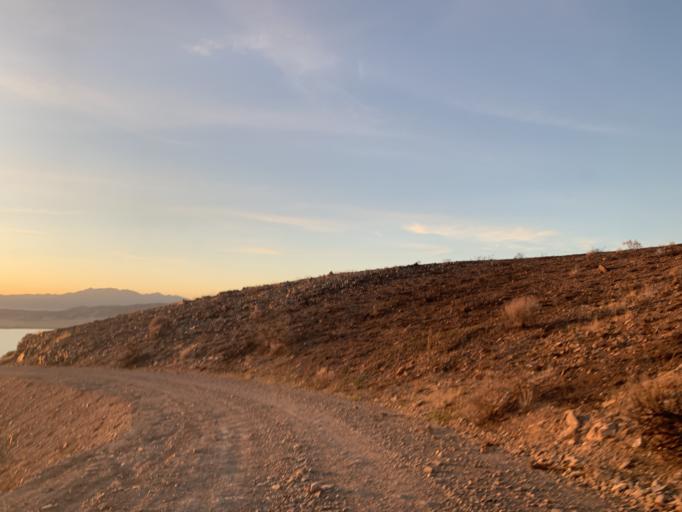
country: US
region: Utah
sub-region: Utah County
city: West Mountain
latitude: 40.1086
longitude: -111.8209
